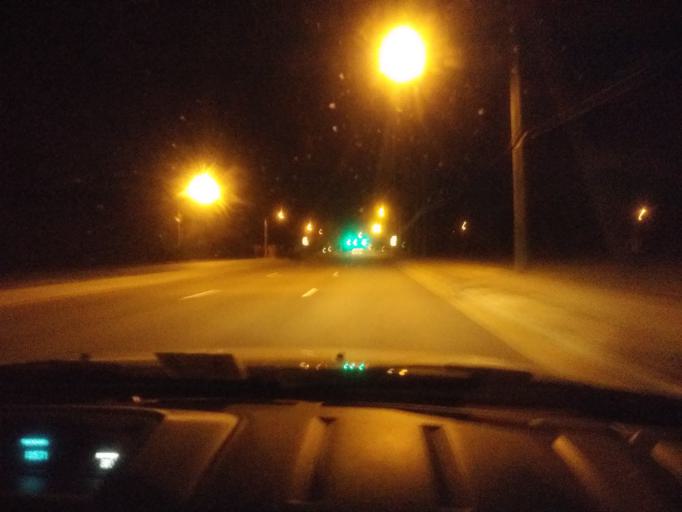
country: US
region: Virginia
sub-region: City of Chesapeake
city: Chesapeake
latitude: 36.7718
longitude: -76.2022
